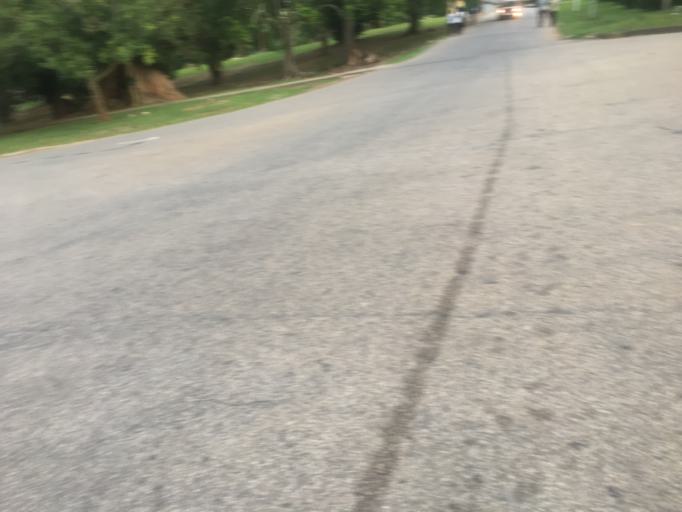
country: GH
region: Ashanti
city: Kumasi
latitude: 6.6752
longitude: -1.5724
